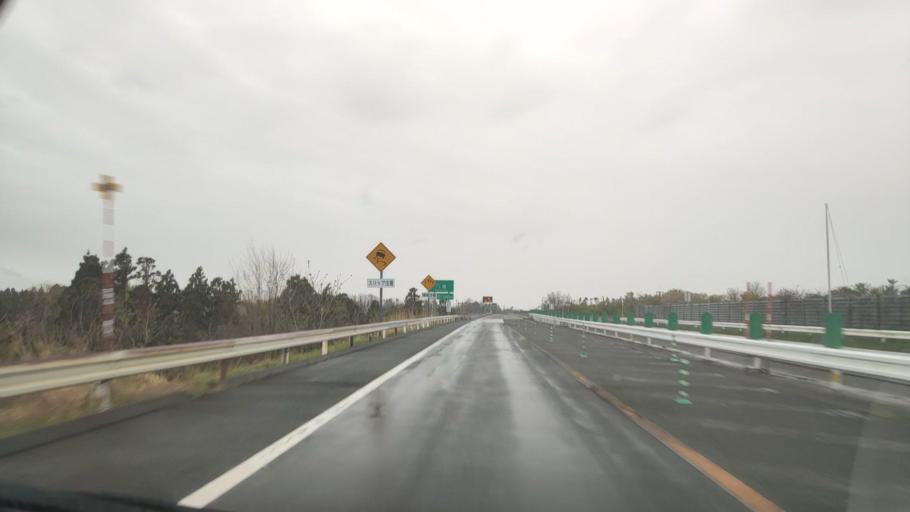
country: JP
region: Akita
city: Noshiromachi
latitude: 40.1267
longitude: 140.0125
